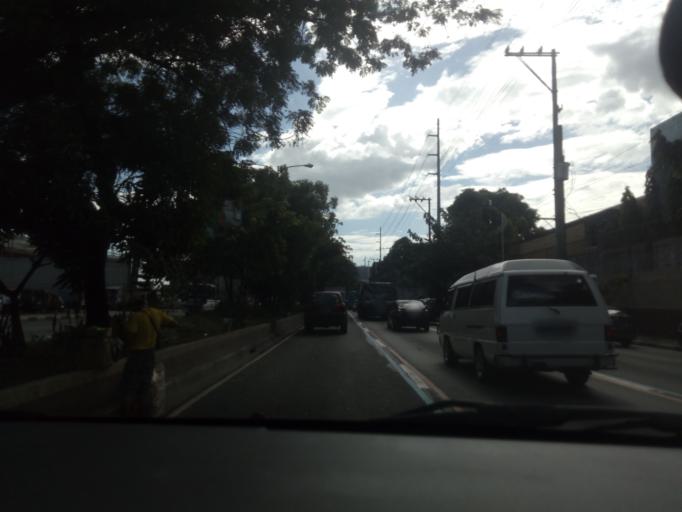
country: PH
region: Metro Manila
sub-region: Pasig
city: Pasig City
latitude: 14.5808
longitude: 121.0755
